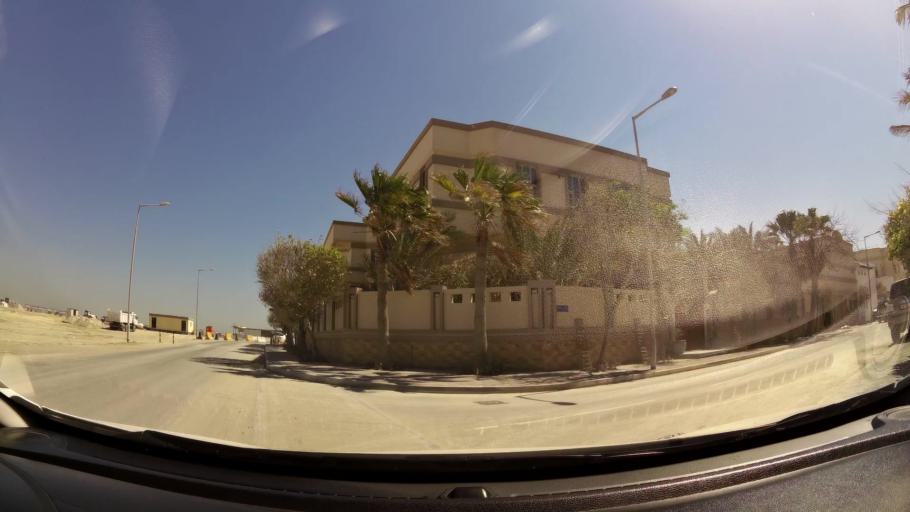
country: BH
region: Muharraq
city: Al Muharraq
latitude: 26.2821
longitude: 50.6021
